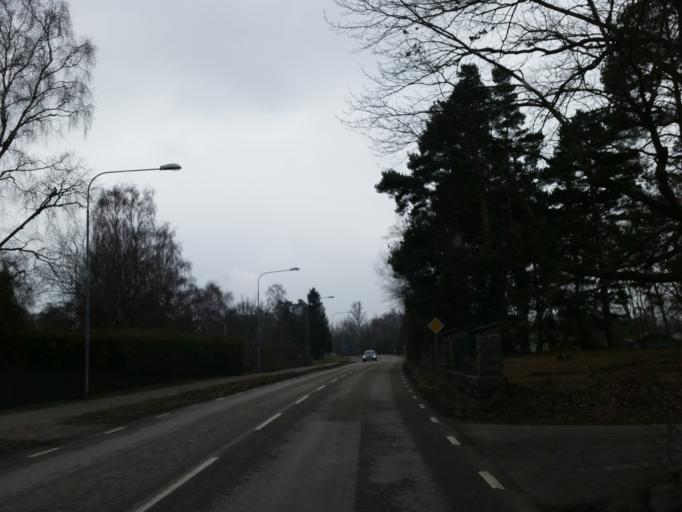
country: SE
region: Kalmar
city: Faerjestaden
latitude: 56.6420
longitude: 16.4645
